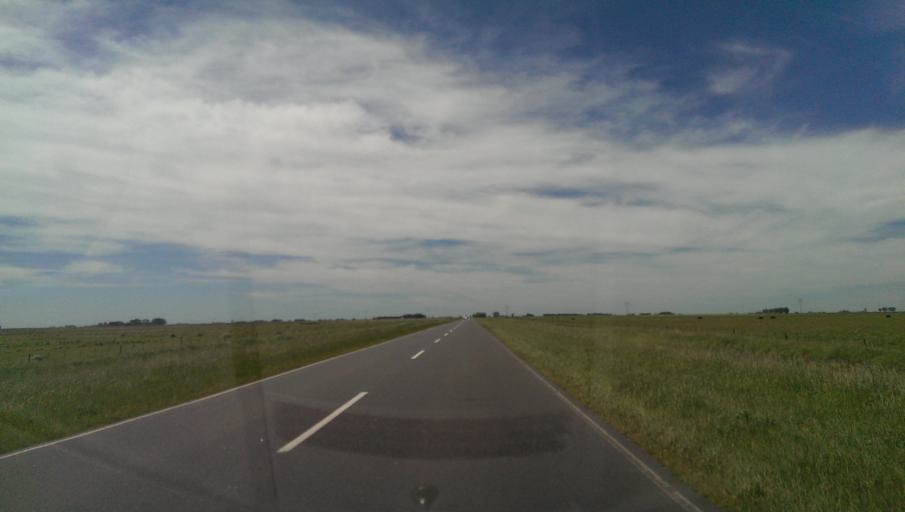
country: AR
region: Buenos Aires
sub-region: Partido de Laprida
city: Laprida
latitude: -37.2383
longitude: -60.7467
